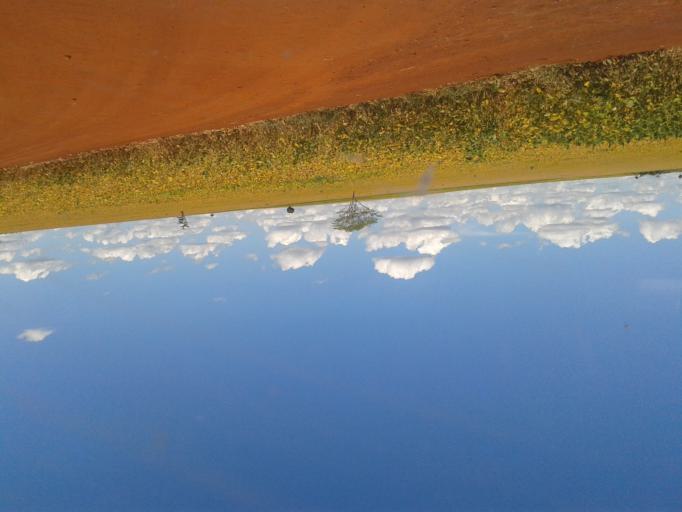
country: BR
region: Minas Gerais
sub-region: Capinopolis
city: Capinopolis
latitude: -18.6490
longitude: -49.5686
